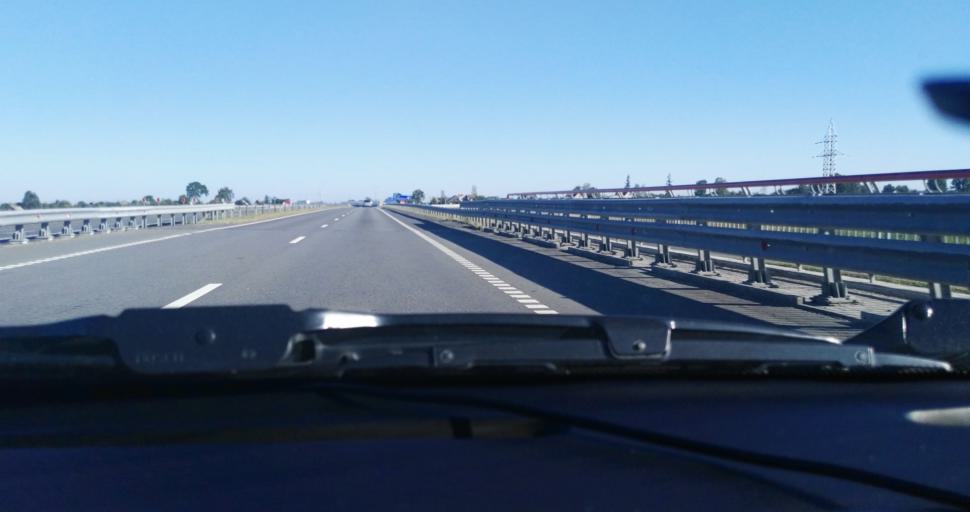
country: BY
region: Gomel
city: Buda-Kashalyova
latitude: 52.5146
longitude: 30.6292
